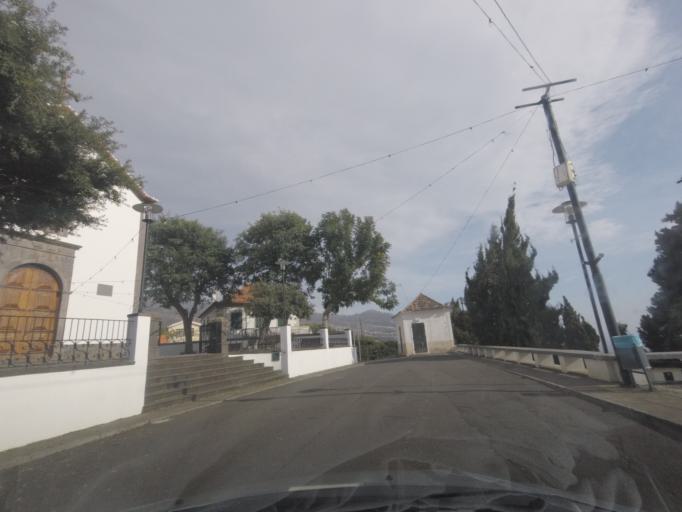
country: PT
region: Madeira
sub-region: Calheta
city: Estreito da Calheta
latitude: 32.7361
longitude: -17.1889
